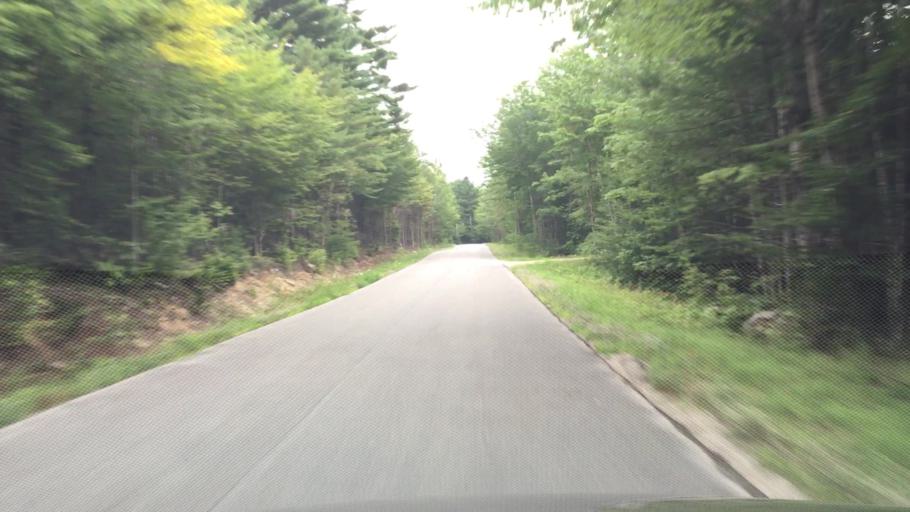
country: US
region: Maine
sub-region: Waldo County
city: Stockton Springs
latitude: 44.5202
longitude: -68.8791
